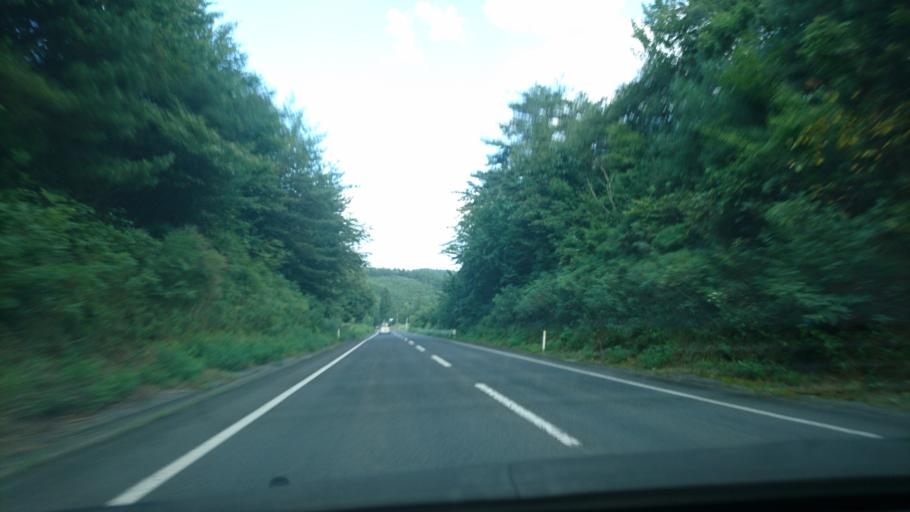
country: JP
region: Iwate
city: Mizusawa
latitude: 39.0307
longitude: 141.2795
